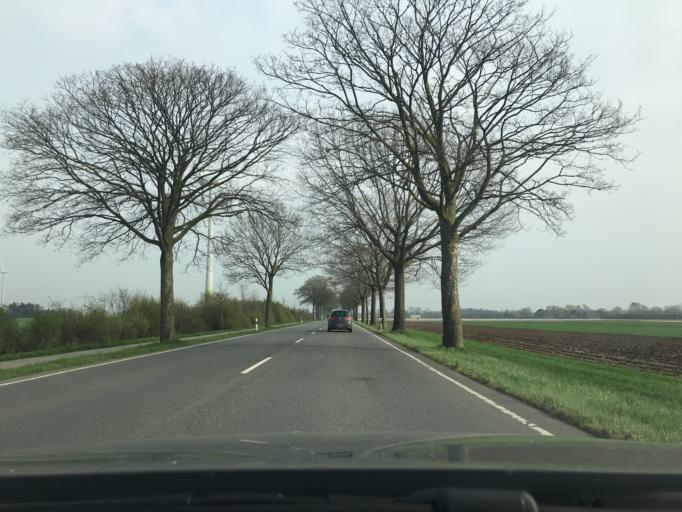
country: DE
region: North Rhine-Westphalia
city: Geldern
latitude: 51.4728
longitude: 6.3518
